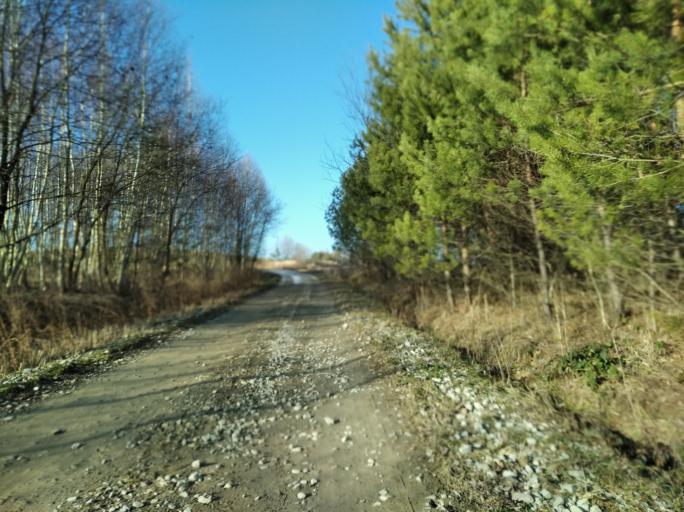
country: PL
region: Subcarpathian Voivodeship
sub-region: Powiat strzyzowski
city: Jawornik
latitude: 49.8364
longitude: 21.8576
